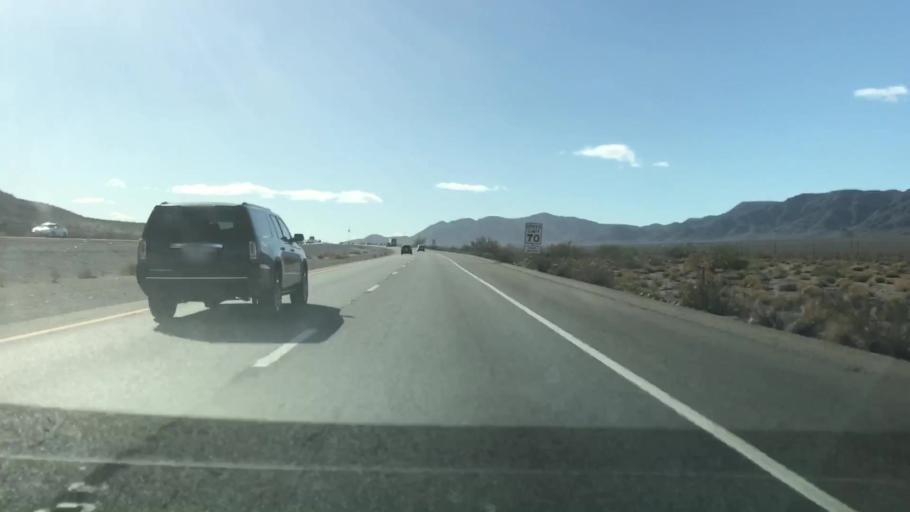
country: US
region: California
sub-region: San Bernardino County
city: Fort Irwin
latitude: 35.1888
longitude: -116.1598
